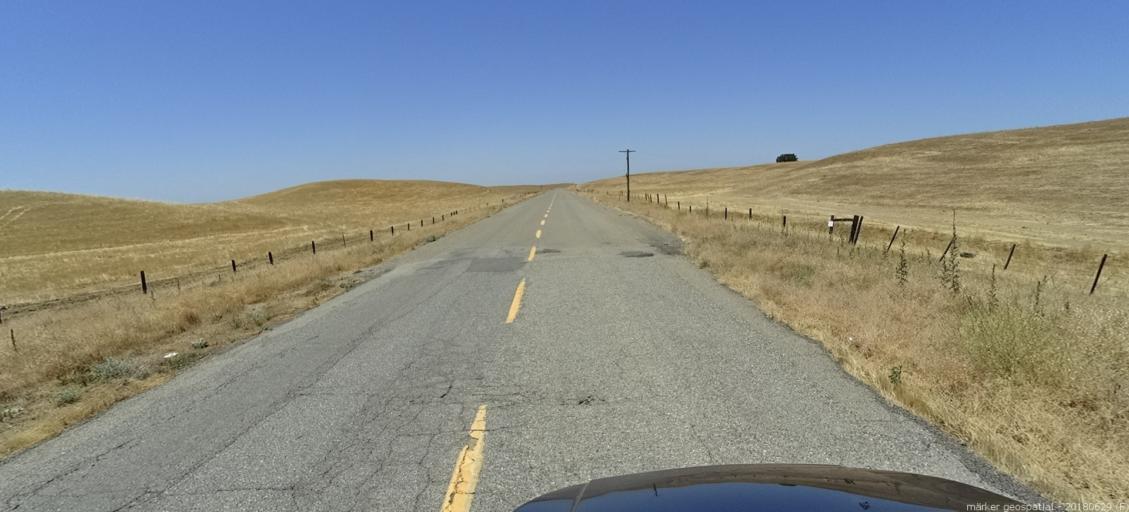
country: US
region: California
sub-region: Madera County
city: Bonadelle Ranchos-Madera Ranchos
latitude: 37.0413
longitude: -119.9283
